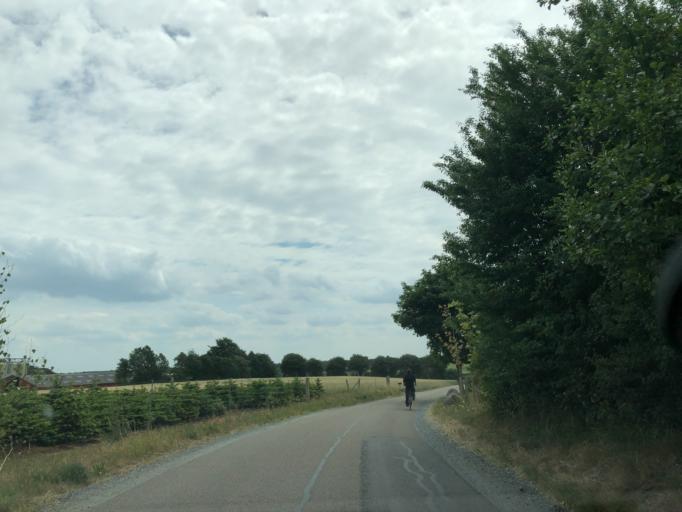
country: DK
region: Central Jutland
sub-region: Silkeborg Kommune
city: Svejbaek
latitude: 56.2041
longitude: 9.6900
